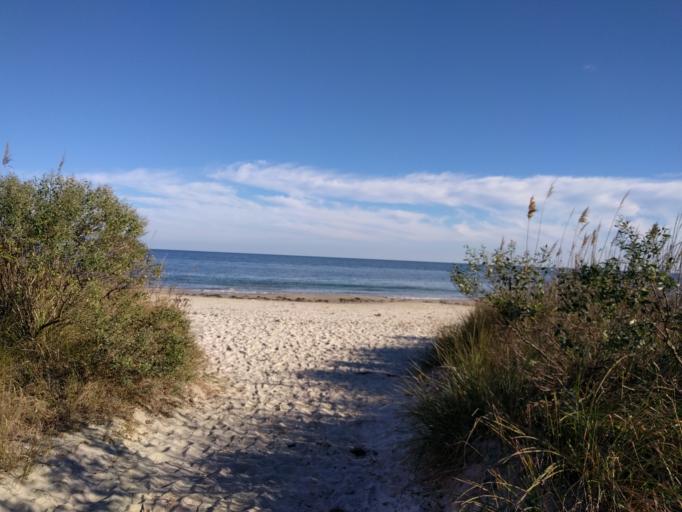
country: US
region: Virginia
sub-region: City of Hampton
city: East Hampton
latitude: 37.0825
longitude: -76.2747
